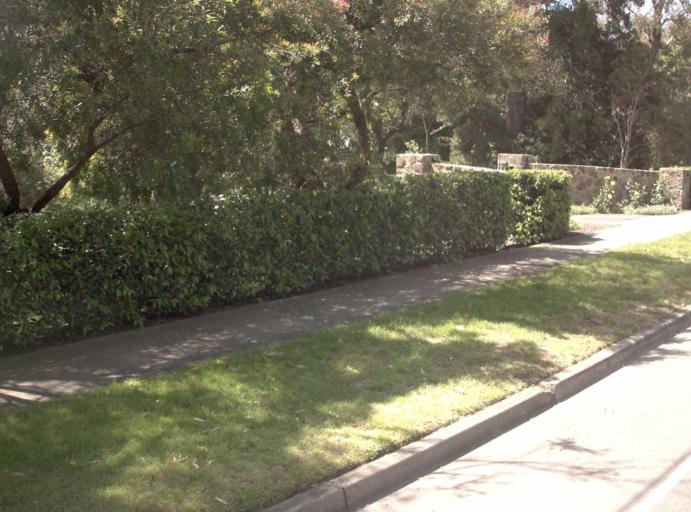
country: AU
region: Victoria
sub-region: Whitehorse
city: Blackburn South
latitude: -37.8304
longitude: 145.1546
